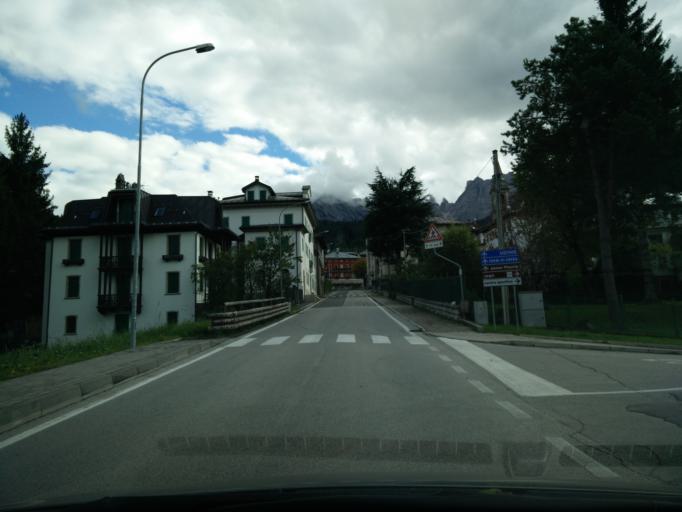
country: IT
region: Veneto
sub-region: Provincia di Belluno
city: Lorenzago di Cadore
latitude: 46.4817
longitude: 12.4573
